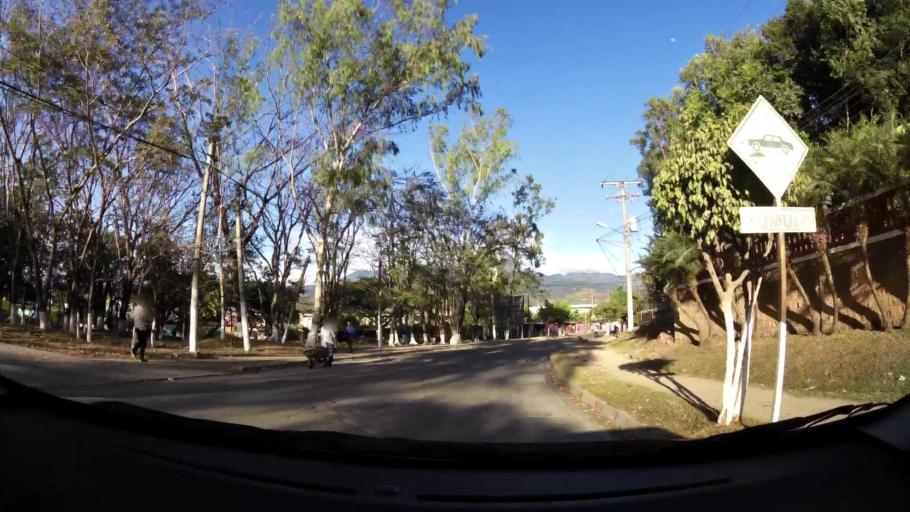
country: SV
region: Santa Ana
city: Metapan
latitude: 14.3290
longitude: -89.4530
